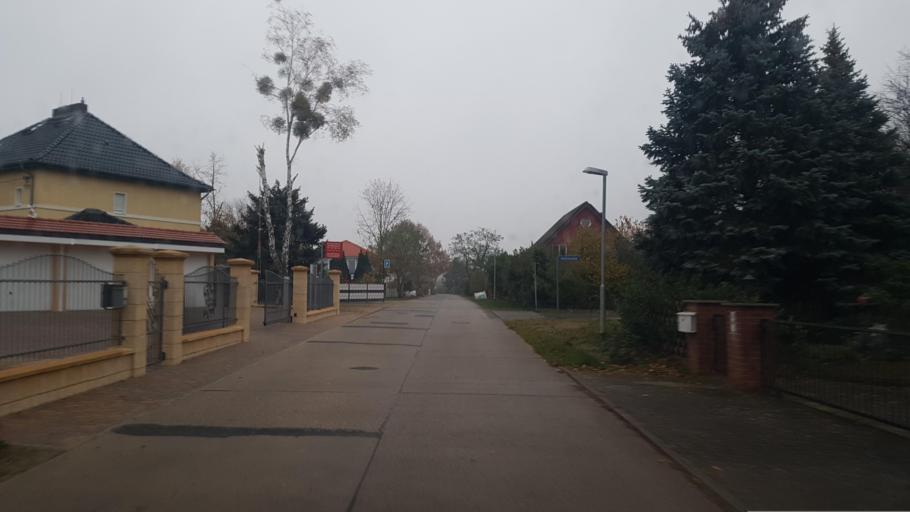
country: DE
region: Brandenburg
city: Michendorf
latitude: 52.3138
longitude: 13.0153
